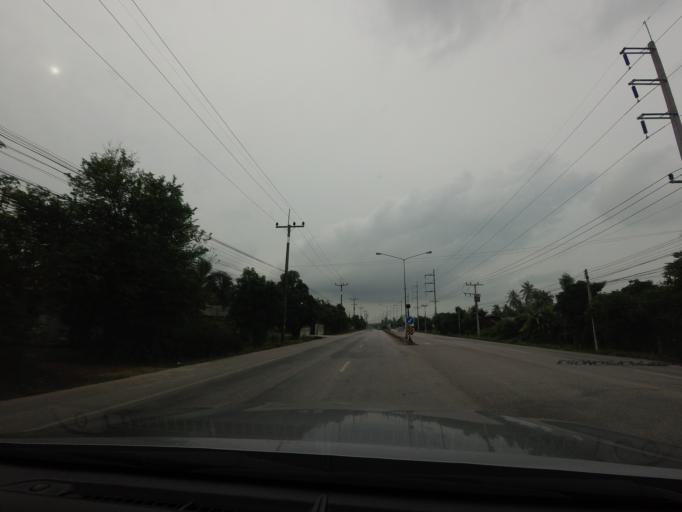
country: TH
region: Songkhla
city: Sathing Phra
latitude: 7.4075
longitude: 100.4620
